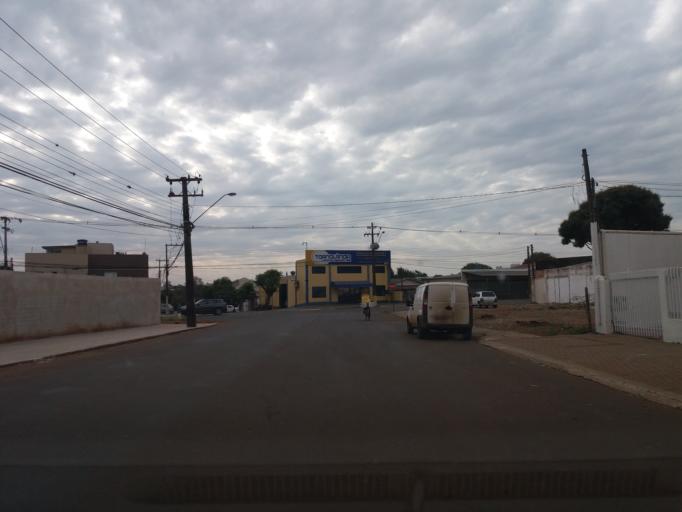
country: BR
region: Parana
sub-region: Cascavel
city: Cascavel
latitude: -24.9818
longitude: -53.4646
